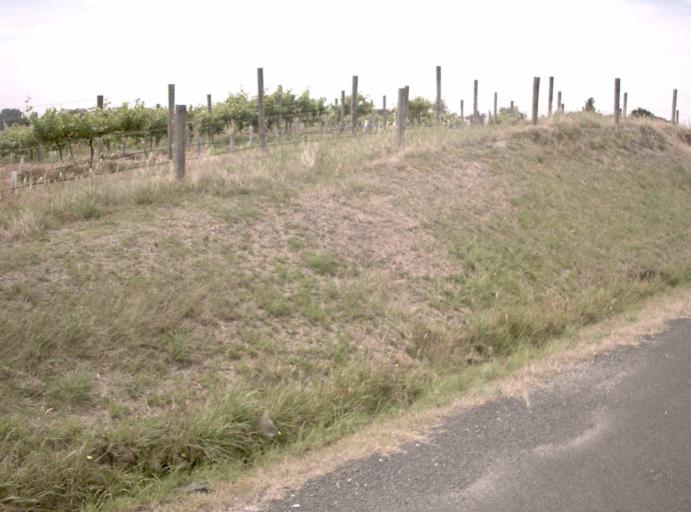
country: AU
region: Victoria
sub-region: Mornington Peninsula
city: Tyabb
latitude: -38.2354
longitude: 145.2155
